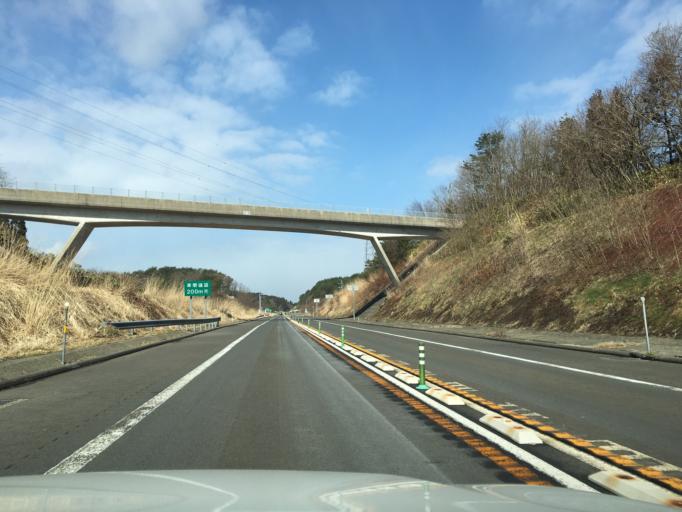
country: JP
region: Akita
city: Akita
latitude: 39.7579
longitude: 140.1343
